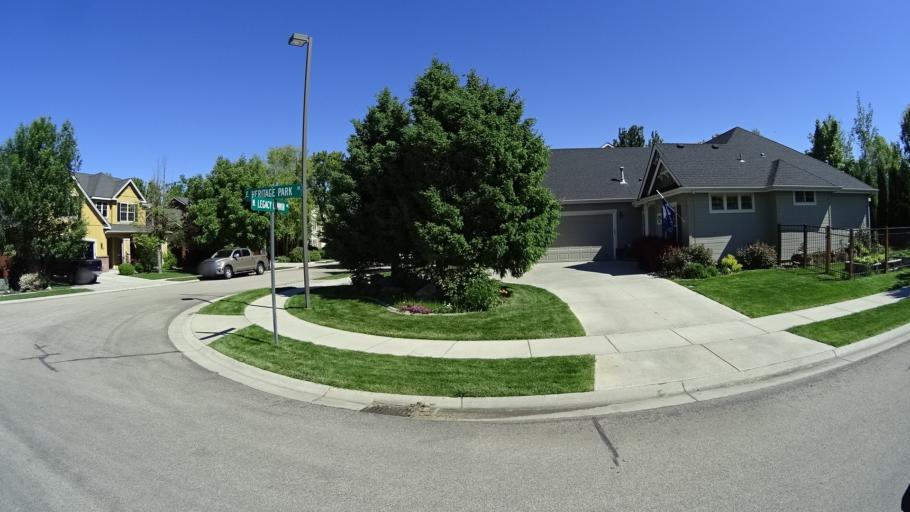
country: US
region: Idaho
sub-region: Ada County
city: Meridian
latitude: 43.6393
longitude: -116.3827
